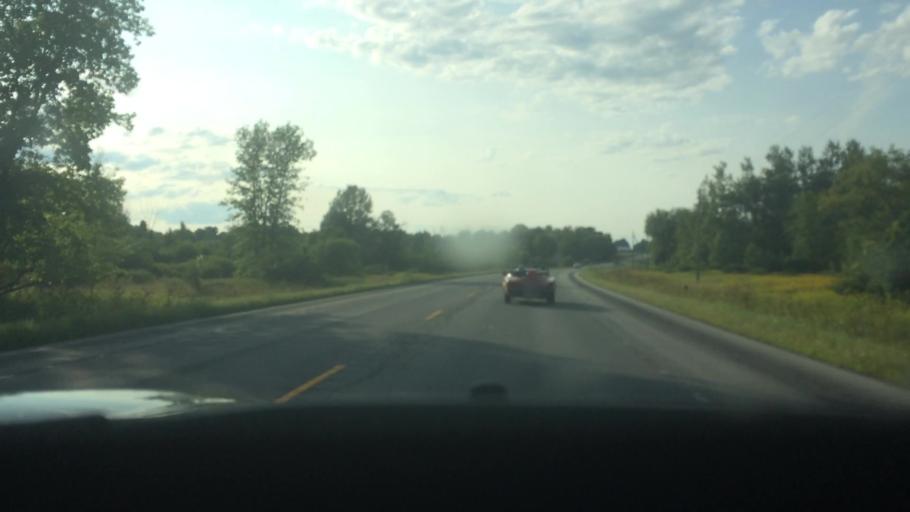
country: US
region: New York
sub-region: St. Lawrence County
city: Canton
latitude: 44.6211
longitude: -75.2293
